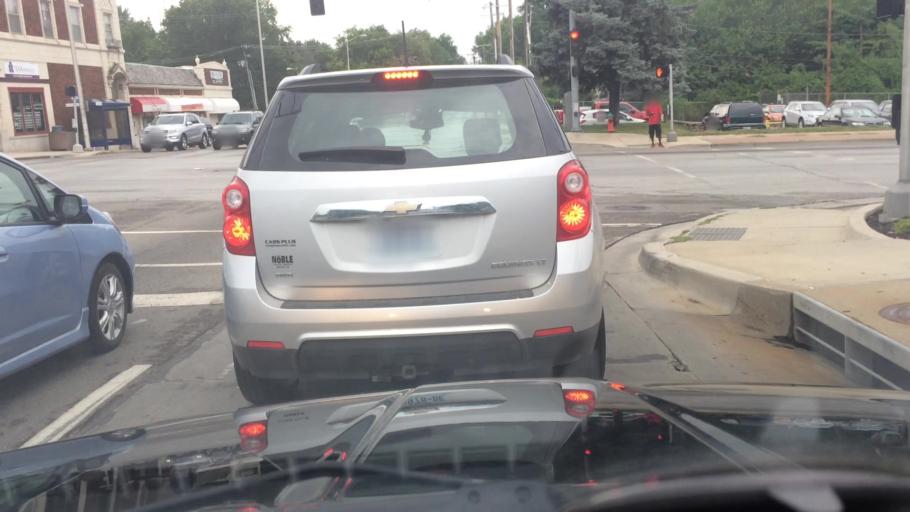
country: US
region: Kansas
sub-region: Johnson County
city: Leawood
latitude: 38.9917
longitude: -94.5754
